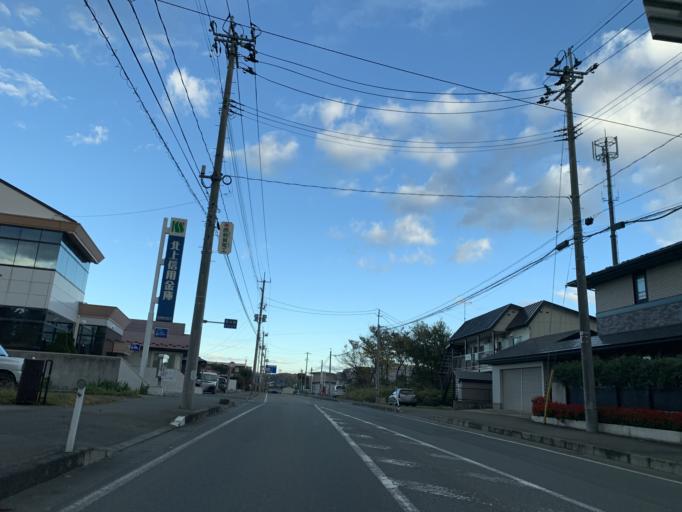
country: JP
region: Iwate
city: Kitakami
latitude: 39.2615
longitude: 141.1000
